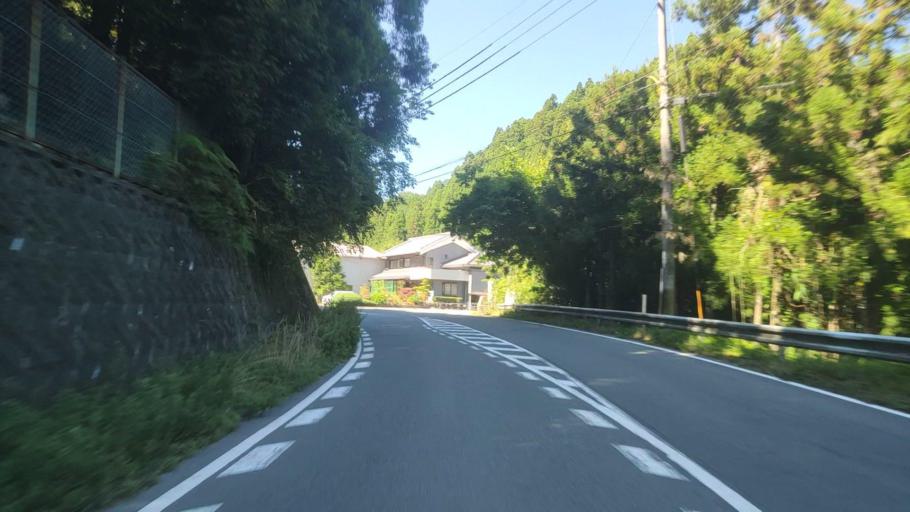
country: JP
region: Nara
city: Yoshino-cho
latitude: 34.4355
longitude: 135.9381
